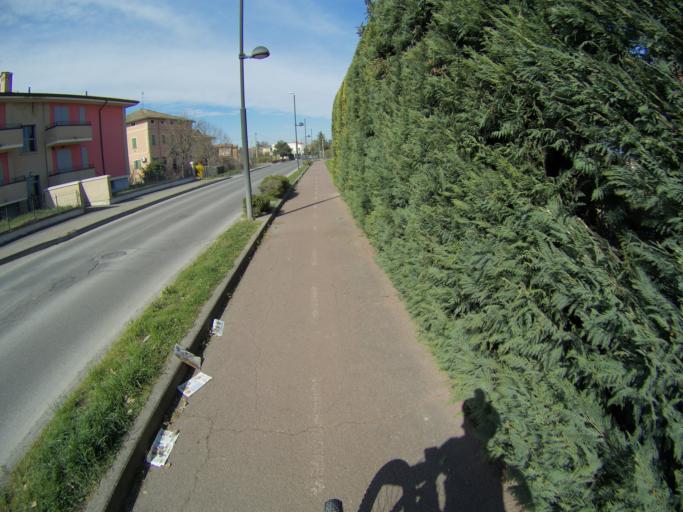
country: IT
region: Emilia-Romagna
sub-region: Provincia di Reggio Emilia
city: Massenzatico
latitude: 44.7296
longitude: 10.6978
